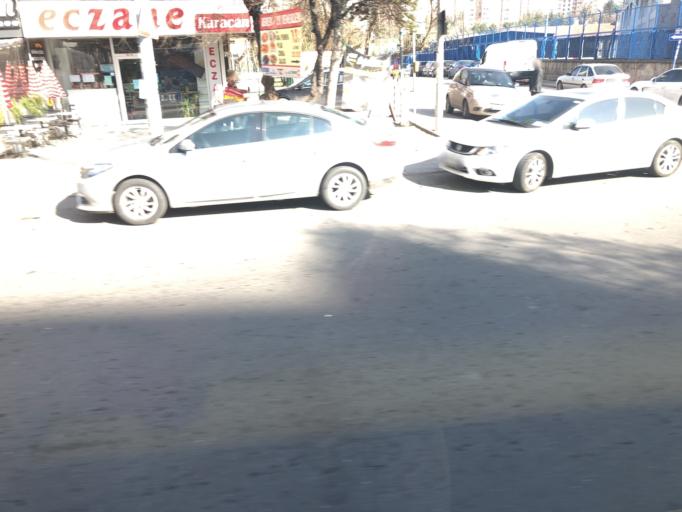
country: TR
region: Ankara
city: Ankara
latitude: 39.9716
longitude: 32.8432
